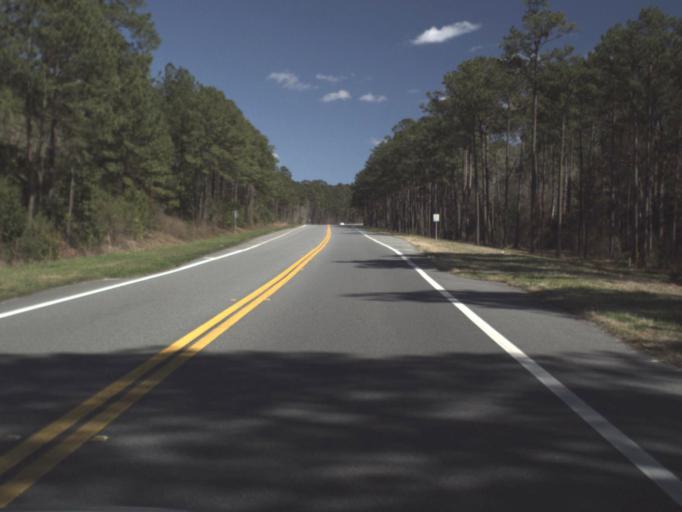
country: US
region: Florida
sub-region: Gadsden County
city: Chattahoochee
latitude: 30.7013
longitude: -84.8232
